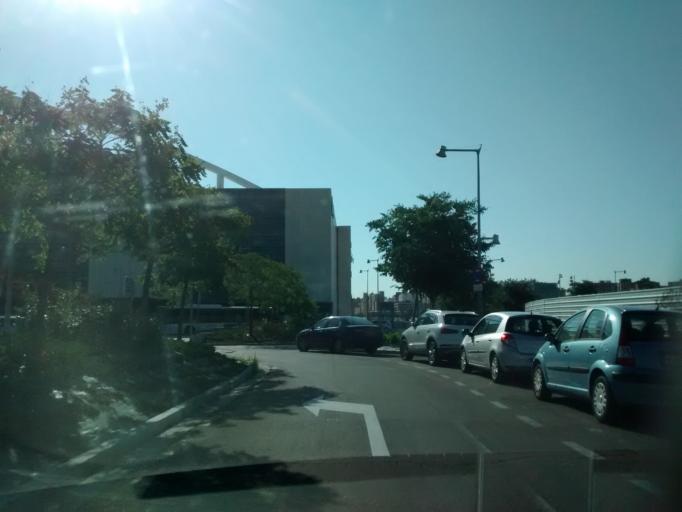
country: ES
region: Aragon
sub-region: Provincia de Zaragoza
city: Delicias
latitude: 41.6591
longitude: -0.9145
